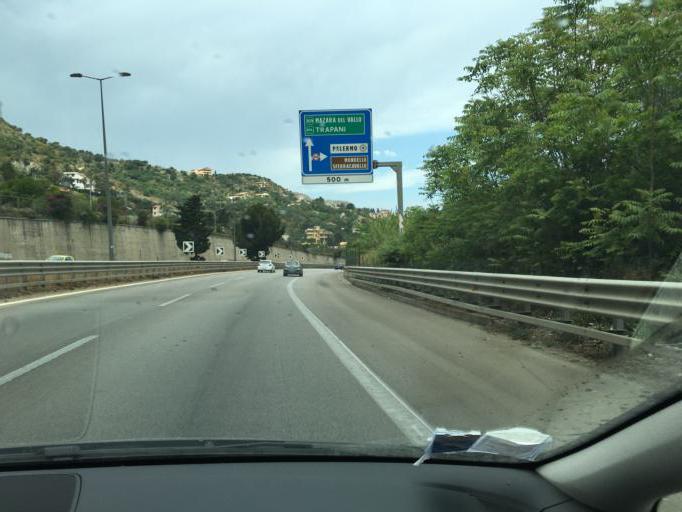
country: IT
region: Sicily
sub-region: Palermo
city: Isola delle Femmine
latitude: 38.1871
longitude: 13.2857
